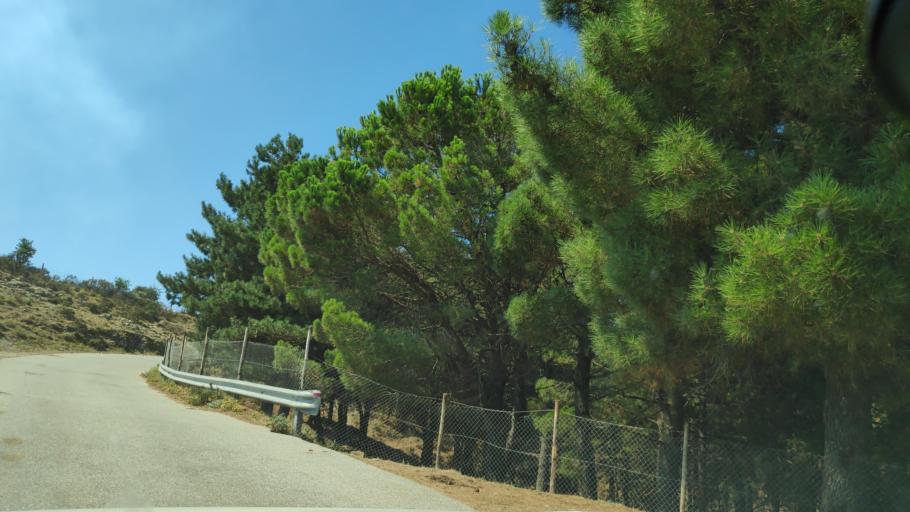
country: IT
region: Calabria
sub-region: Provincia di Reggio Calabria
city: Bova
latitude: 38.0134
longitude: 15.9355
